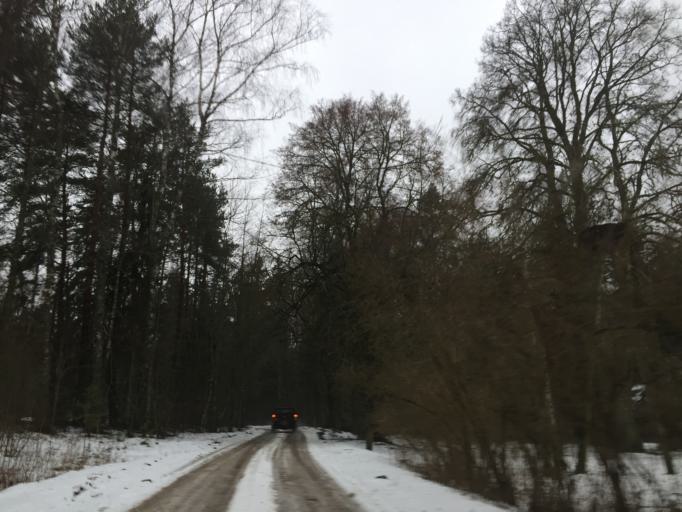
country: LV
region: Incukalns
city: Vangazi
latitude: 57.1260
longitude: 24.5713
